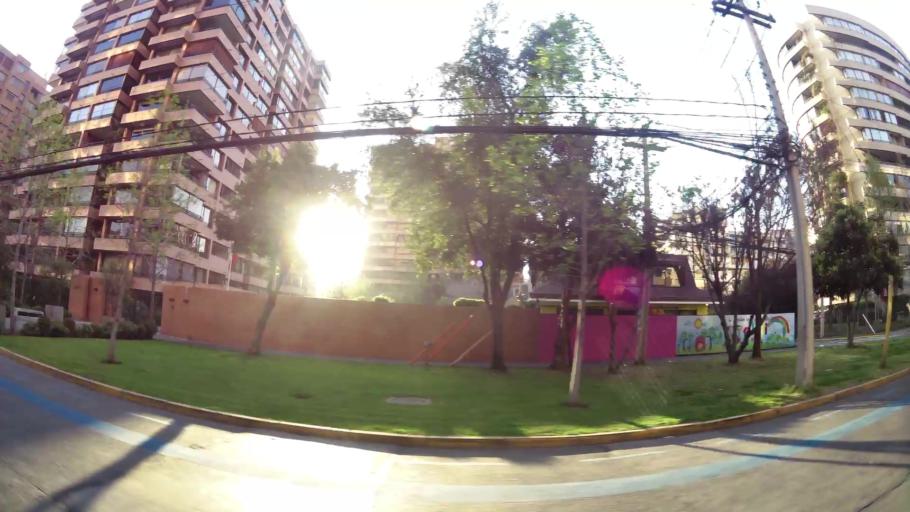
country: CL
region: Santiago Metropolitan
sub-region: Provincia de Santiago
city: Villa Presidente Frei, Nunoa, Santiago, Chile
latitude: -33.4060
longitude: -70.5639
